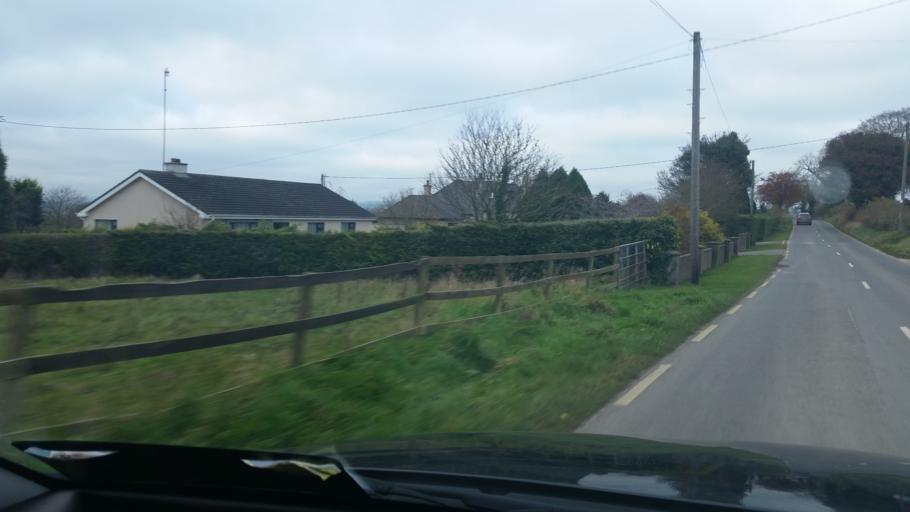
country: IE
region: Leinster
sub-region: Lu
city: Tullyallen
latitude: 53.7035
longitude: -6.4077
